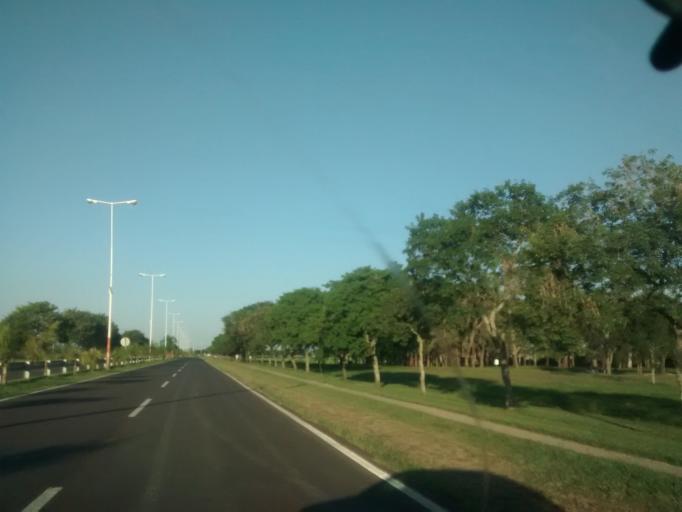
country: AR
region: Chaco
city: Fontana
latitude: -27.4421
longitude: -59.0374
